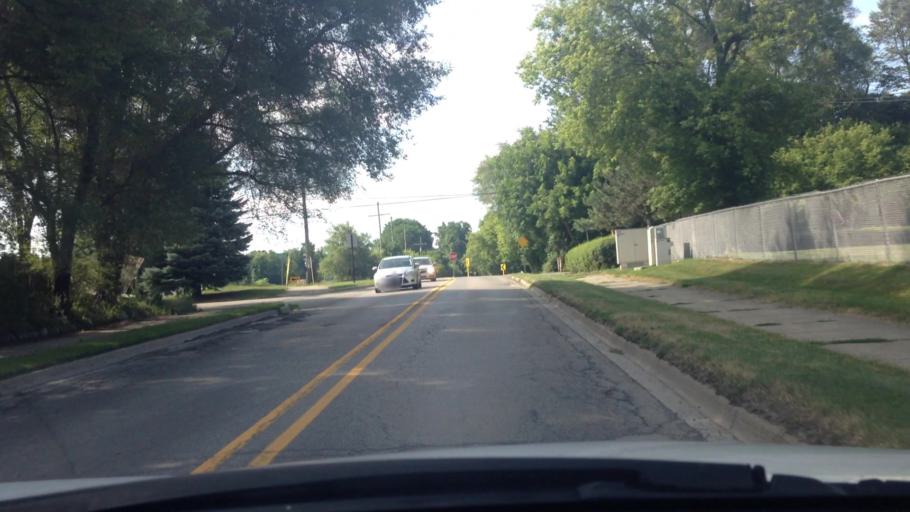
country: US
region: Michigan
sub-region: Oakland County
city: Clarkston
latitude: 42.7646
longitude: -83.3415
